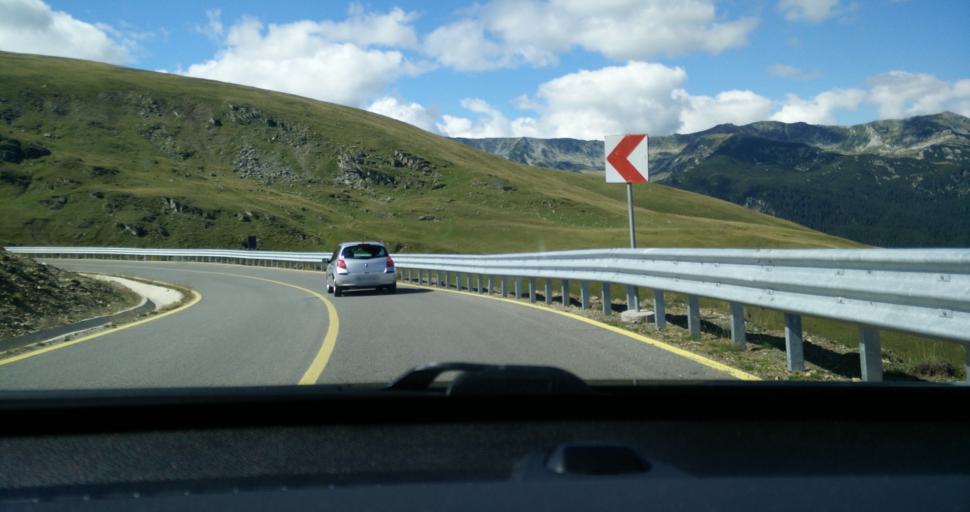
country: RO
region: Gorj
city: Novaci-Straini
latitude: 45.3786
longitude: 23.6496
